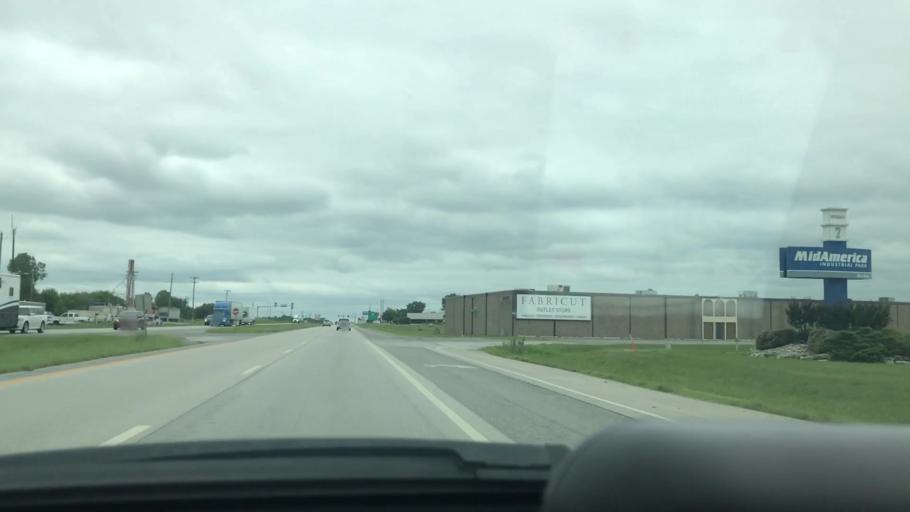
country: US
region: Oklahoma
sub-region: Mayes County
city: Chouteau
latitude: 36.2420
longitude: -95.3372
